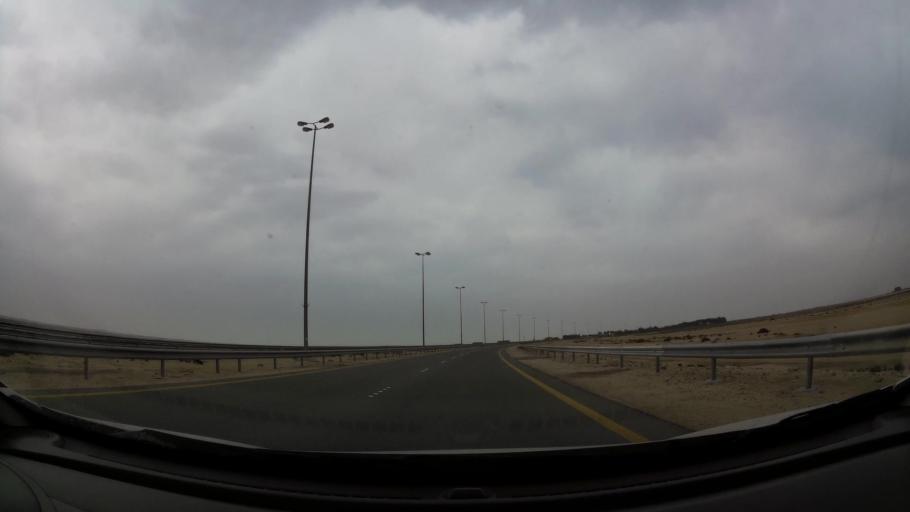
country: BH
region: Central Governorate
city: Dar Kulayb
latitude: 25.9995
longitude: 50.4849
